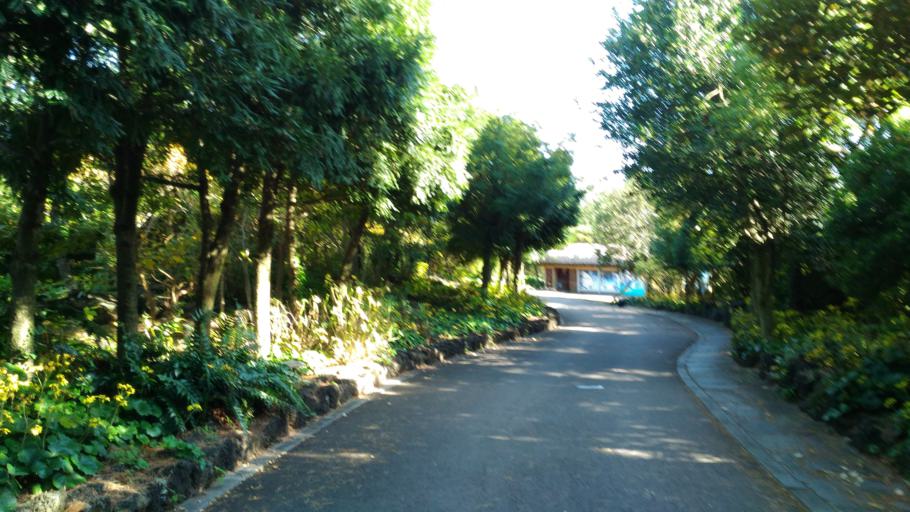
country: KR
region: Jeju-do
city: Seogwipo
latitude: 33.3209
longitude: 126.8427
